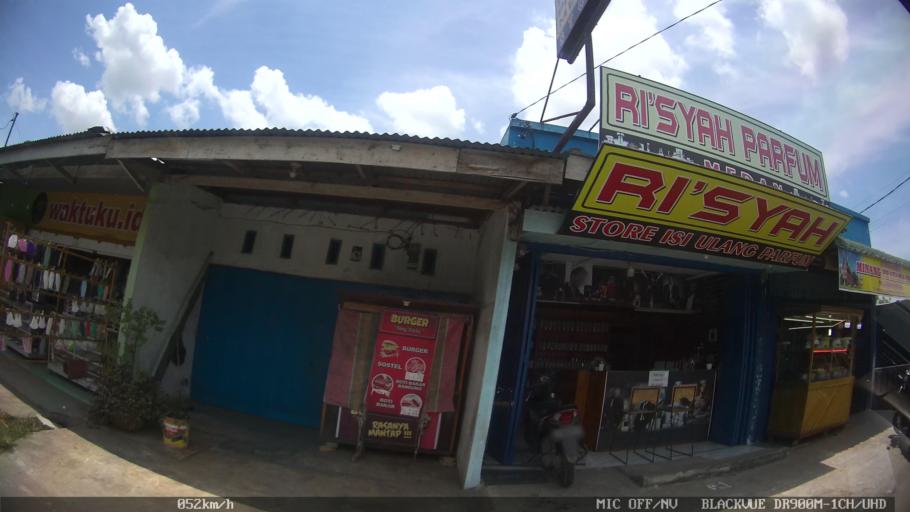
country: ID
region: North Sumatra
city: Binjai
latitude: 3.6114
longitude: 98.5181
